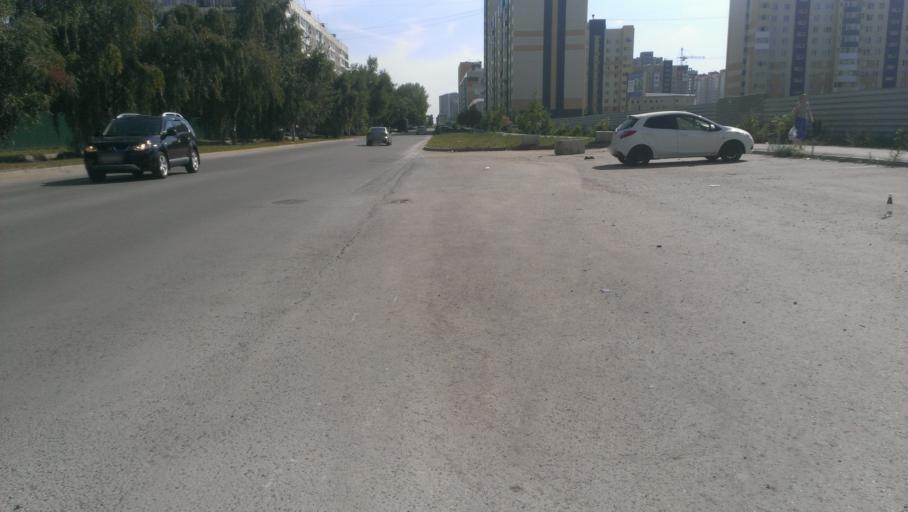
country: RU
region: Altai Krai
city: Novosilikatnyy
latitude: 53.3430
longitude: 83.6622
